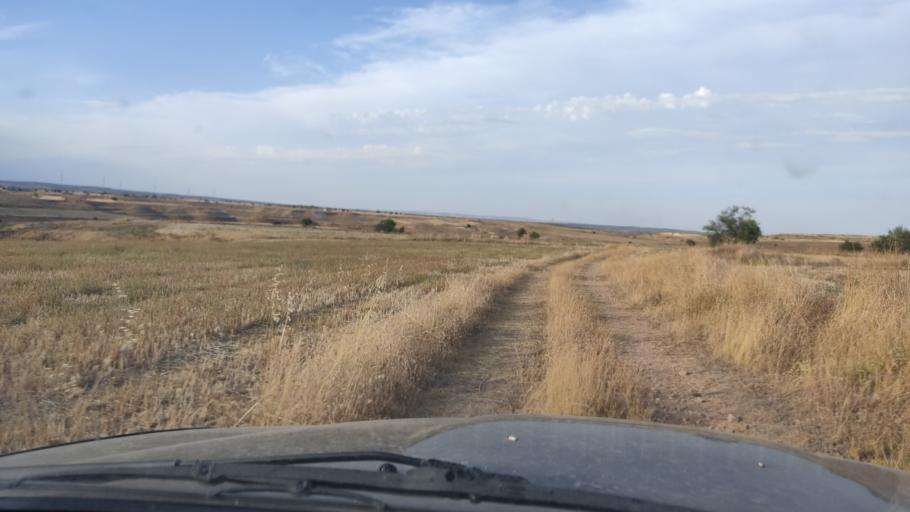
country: ES
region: Aragon
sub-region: Provincia de Teruel
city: Monforte de Moyuela
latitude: 41.0649
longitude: -0.9698
